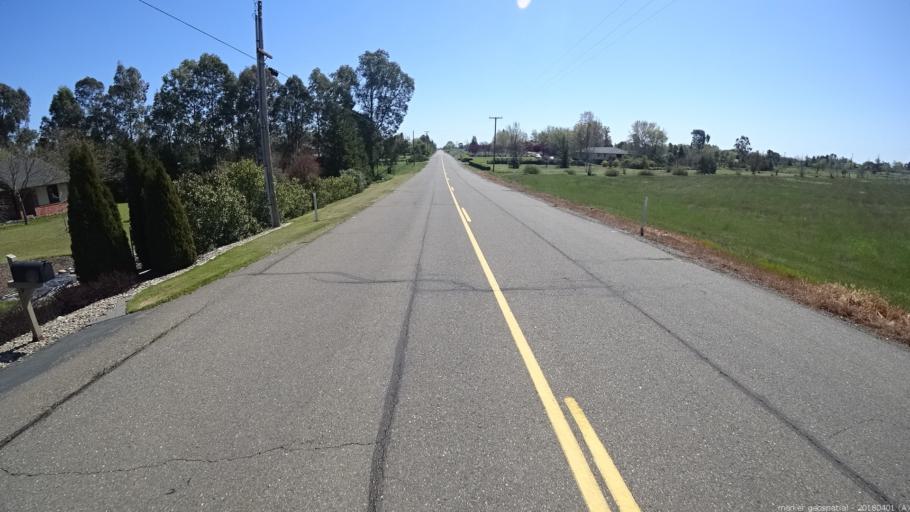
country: US
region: California
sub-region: Sacramento County
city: Wilton
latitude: 38.4186
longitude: -121.2140
